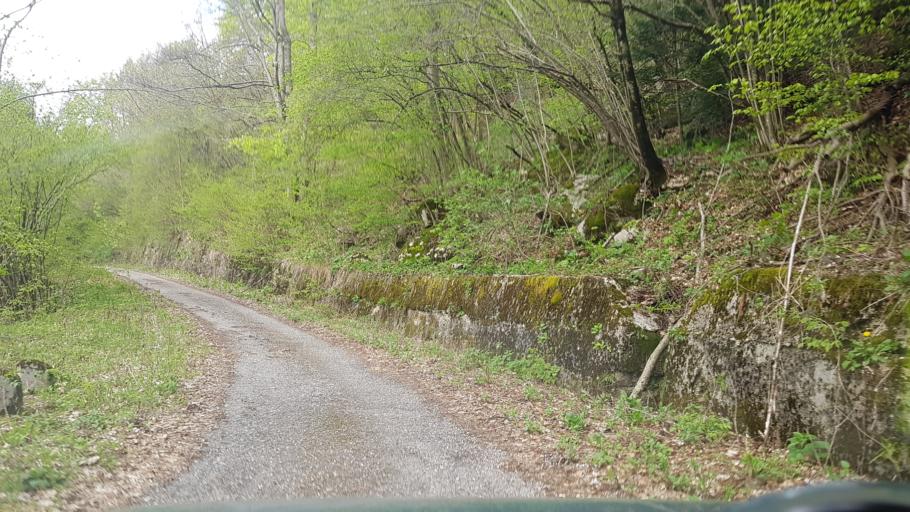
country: IT
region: Friuli Venezia Giulia
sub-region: Provincia di Udine
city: Taipana
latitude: 46.2193
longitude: 13.3557
